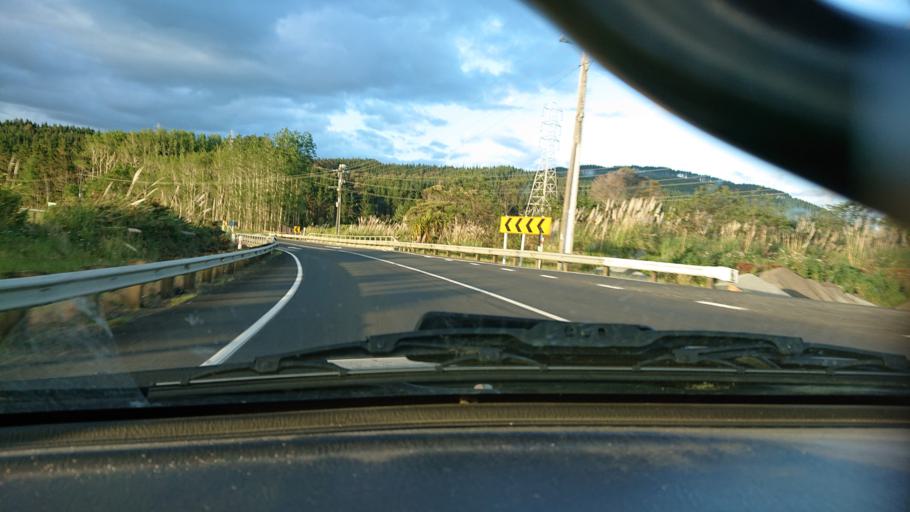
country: NZ
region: Auckland
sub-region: Auckland
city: Parakai
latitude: -36.5079
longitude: 174.4568
